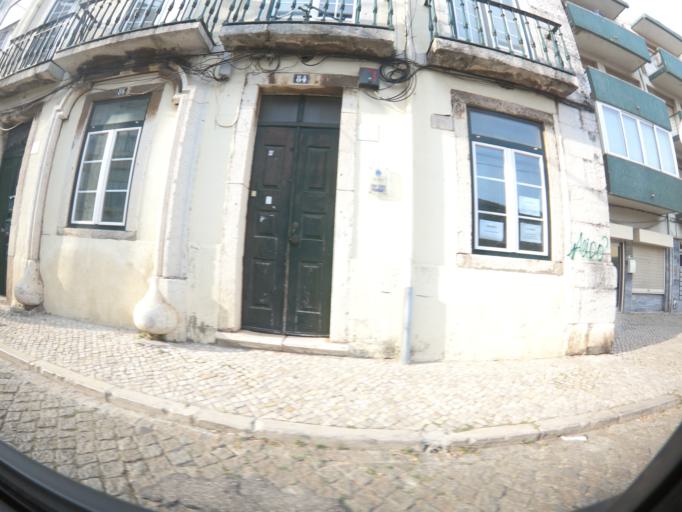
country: PT
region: Lisbon
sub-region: Oeiras
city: Alges
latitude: 38.6964
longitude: -9.2203
